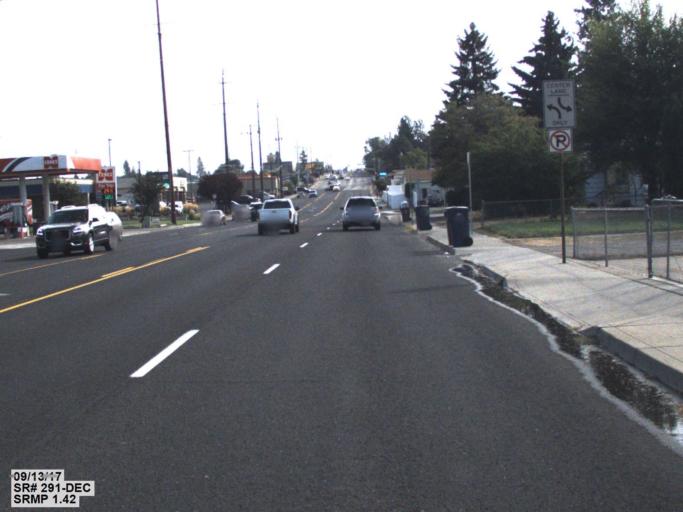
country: US
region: Washington
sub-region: Spokane County
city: Town and Country
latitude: 47.7154
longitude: -117.4415
